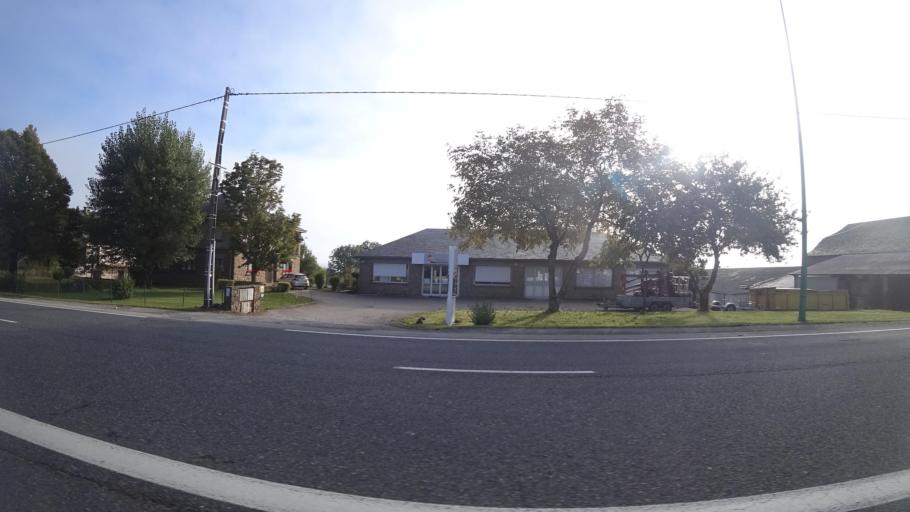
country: FR
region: Midi-Pyrenees
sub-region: Departement de l'Aveyron
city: Luc-la-Primaube
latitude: 44.3105
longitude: 2.5575
